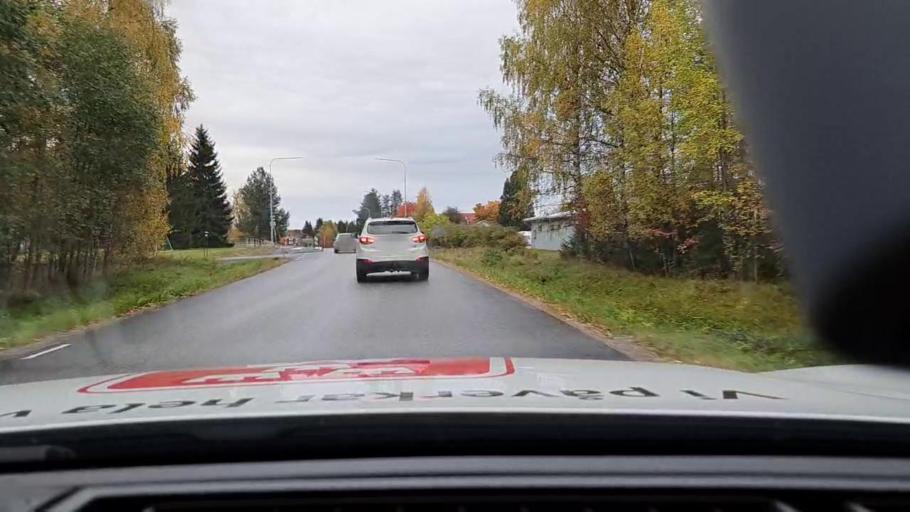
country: SE
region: Norrbotten
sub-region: Bodens Kommun
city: Saevast
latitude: 65.7781
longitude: 21.6923
